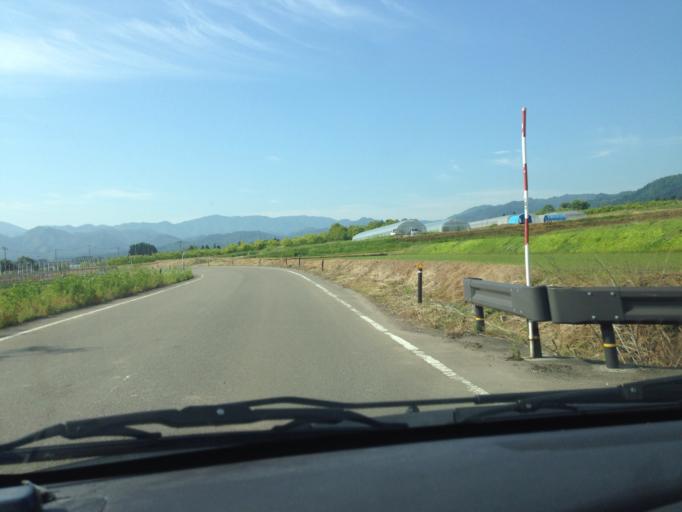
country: JP
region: Fukushima
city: Kitakata
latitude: 37.4691
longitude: 139.8130
